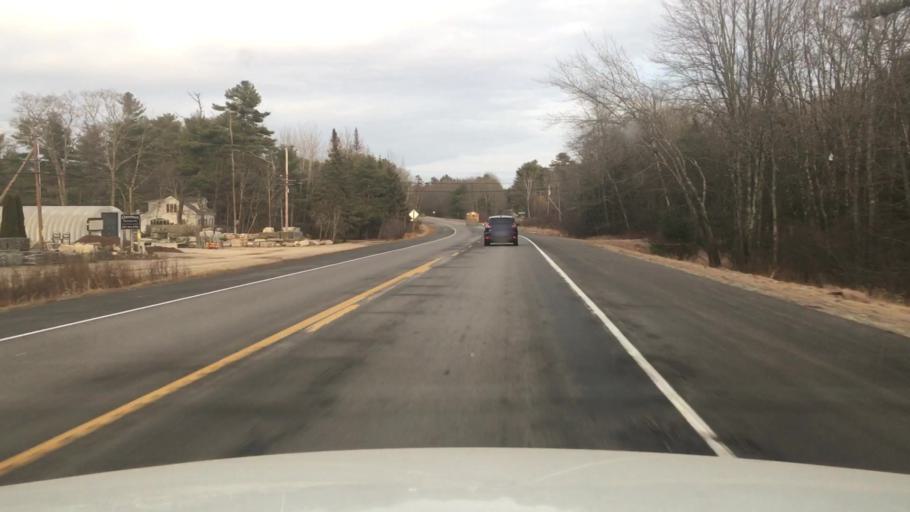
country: US
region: Maine
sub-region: Sagadahoc County
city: Woolwich
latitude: 43.9458
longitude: -69.7532
